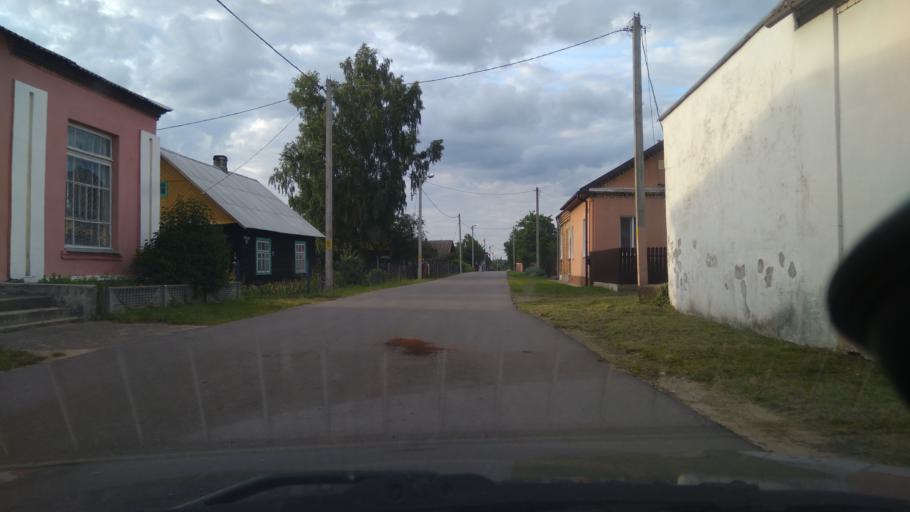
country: BY
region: Grodnenskaya
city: Shchuchin
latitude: 53.5343
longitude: 24.7290
